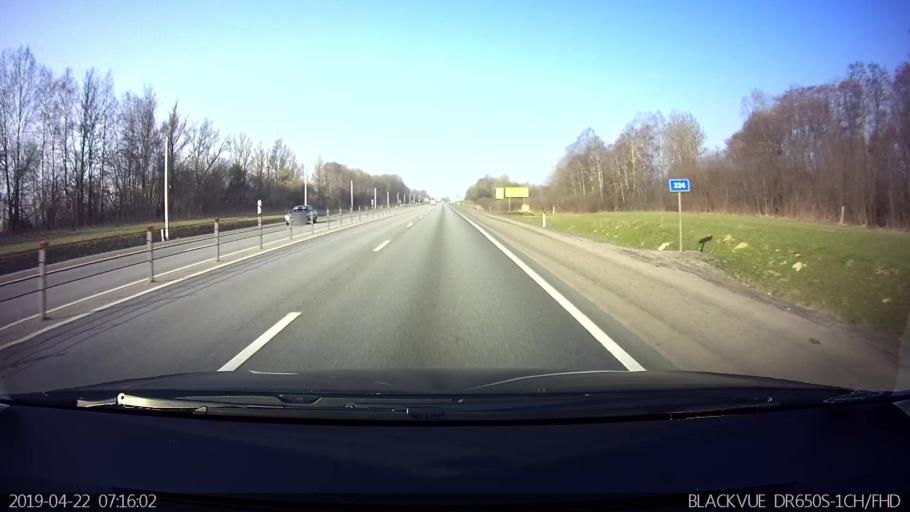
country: RU
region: Smolensk
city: Vyaz'ma
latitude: 55.2528
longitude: 34.3481
